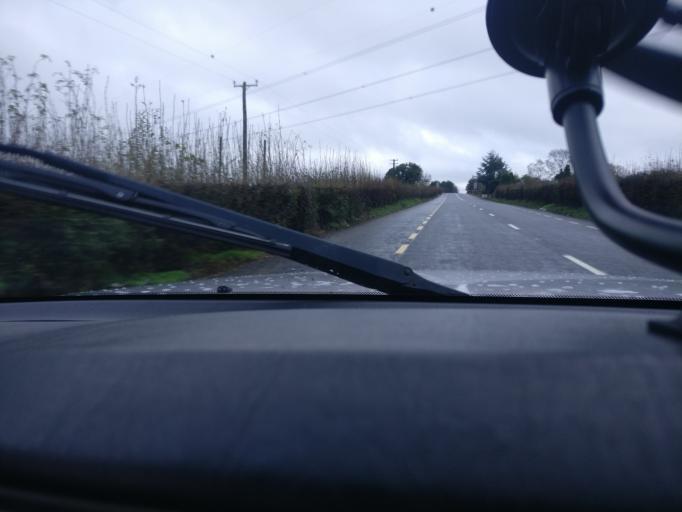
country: IE
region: Leinster
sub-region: An Mhi
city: Enfield
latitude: 53.4232
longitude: -6.8671
